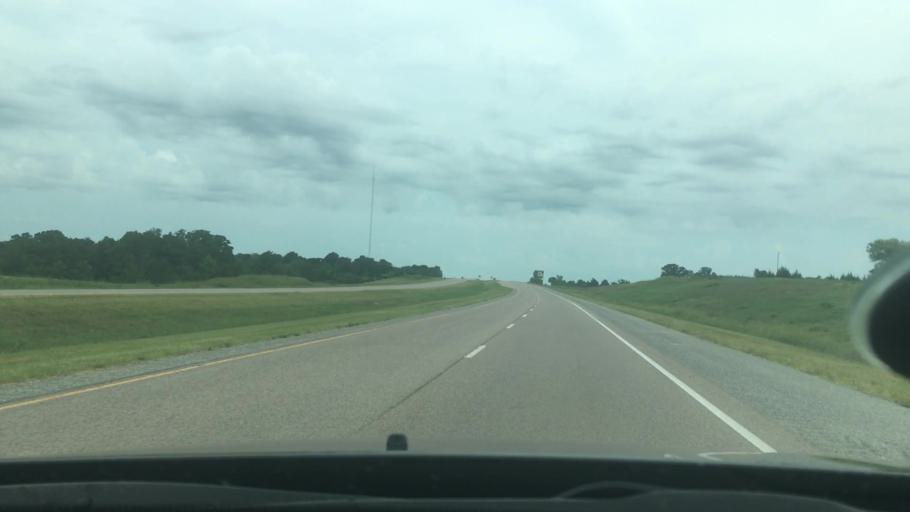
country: US
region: Oklahoma
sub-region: Pontotoc County
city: Byng
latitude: 34.8860
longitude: -96.6753
